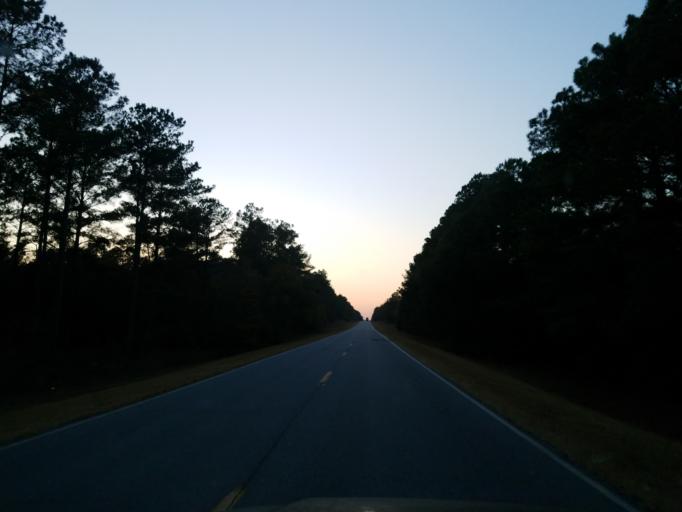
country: US
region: Georgia
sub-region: Turner County
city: Ashburn
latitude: 31.7211
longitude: -83.4604
